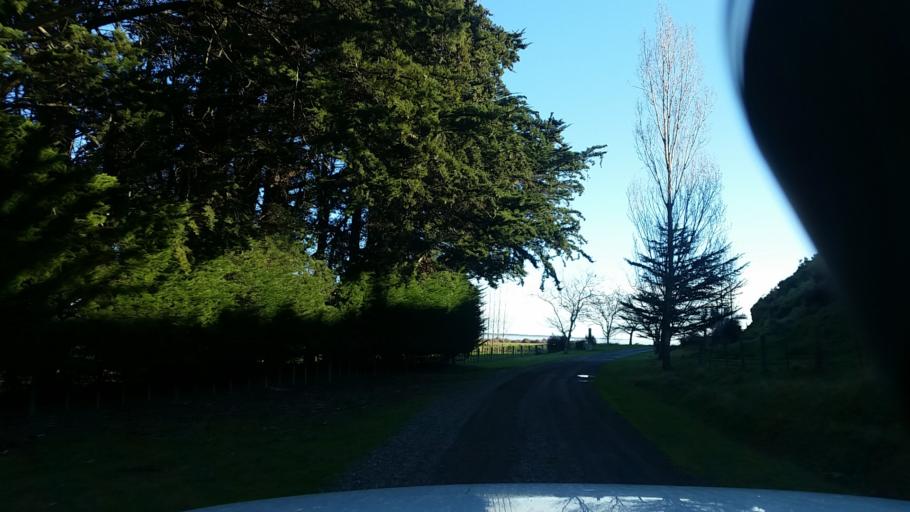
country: NZ
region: Canterbury
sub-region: Selwyn District
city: Lincoln
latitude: -43.7860
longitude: 172.6629
